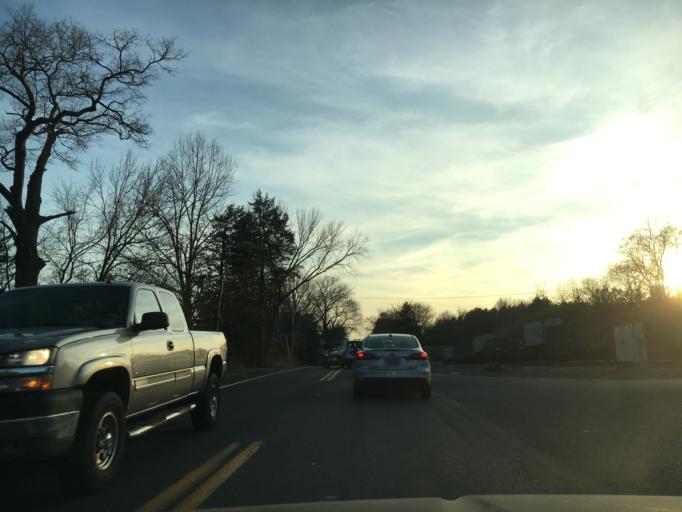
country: US
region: Virginia
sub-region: Culpeper County
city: Culpeper
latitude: 38.4102
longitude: -78.0092
